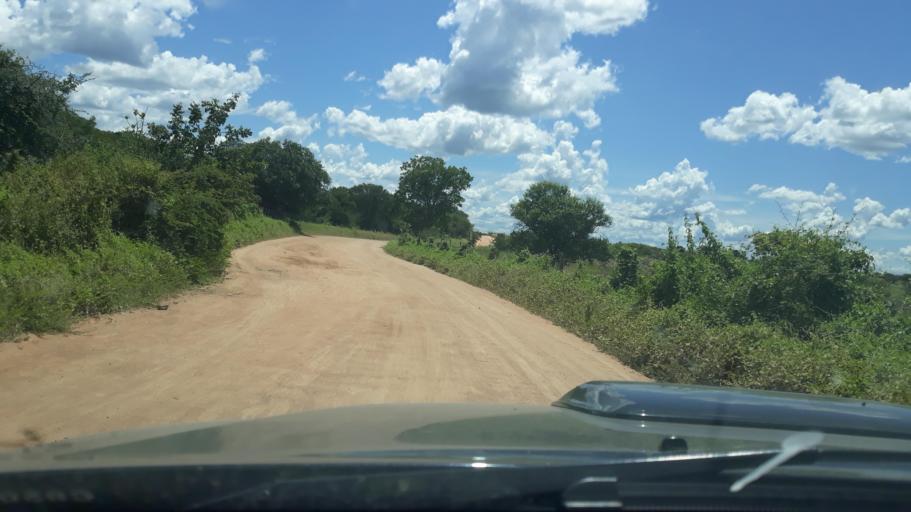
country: BR
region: Bahia
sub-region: Riacho De Santana
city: Riacho de Santana
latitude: -13.8999
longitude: -42.8722
